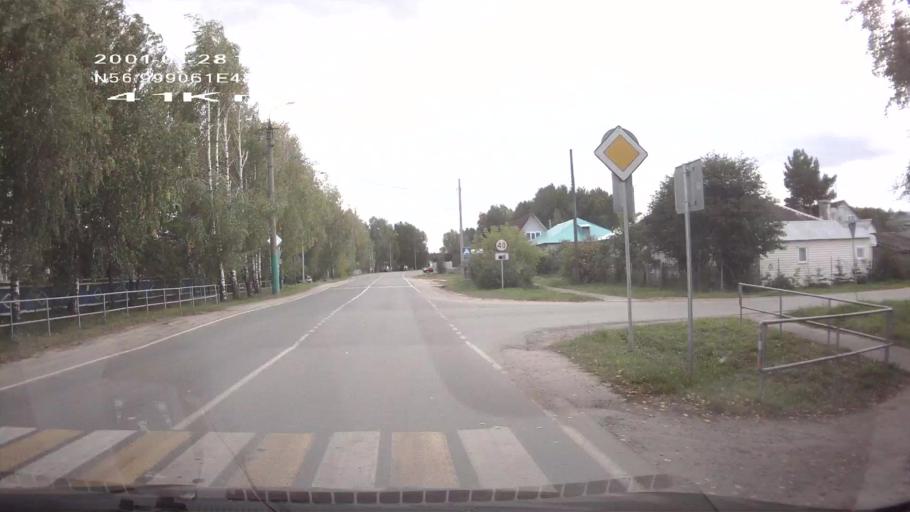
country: RU
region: Mariy-El
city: Kuzhener
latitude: 56.9988
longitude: 48.7403
